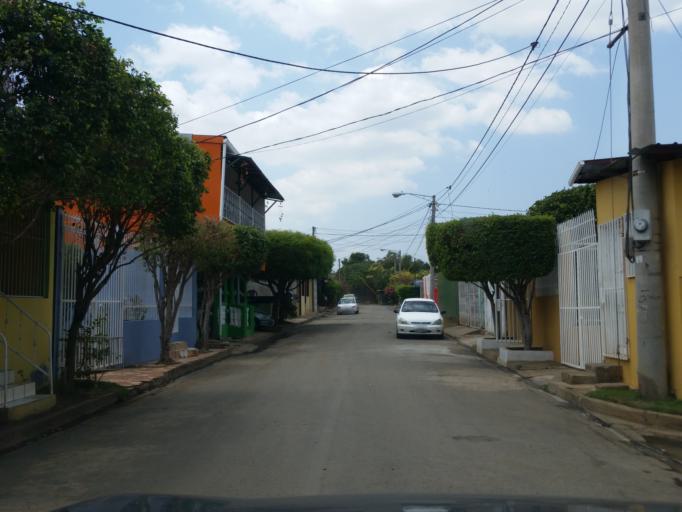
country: NI
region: Managua
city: Managua
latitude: 12.1260
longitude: -86.1902
